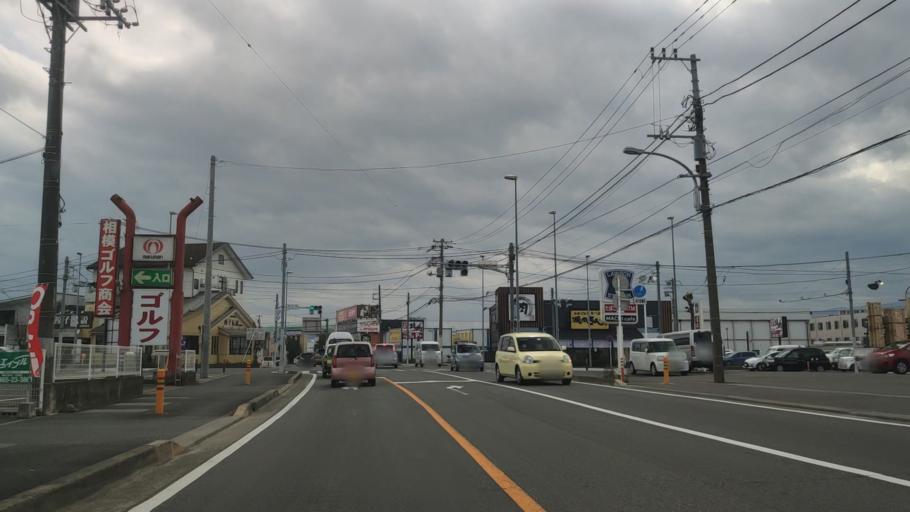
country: JP
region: Kanagawa
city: Odawara
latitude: 35.2904
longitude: 139.1677
